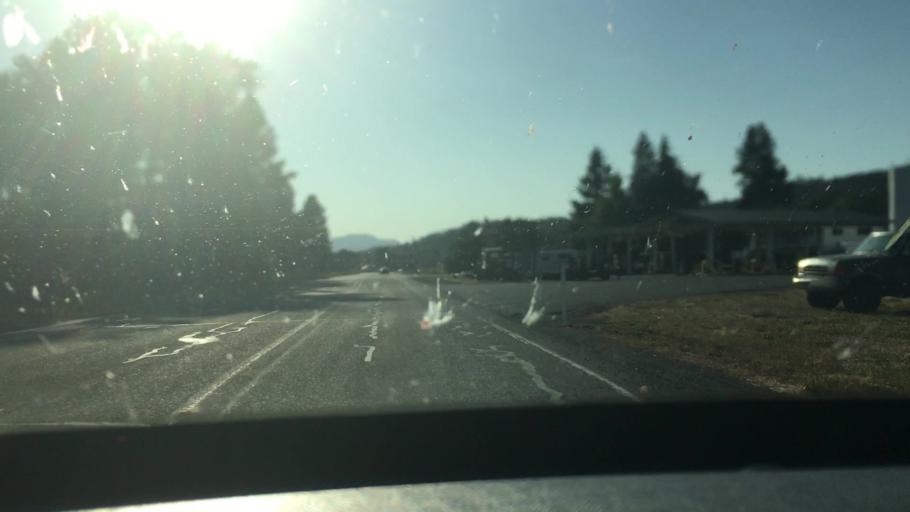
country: US
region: Washington
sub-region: Kittitas County
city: Cle Elum
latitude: 47.1903
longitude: -120.9101
